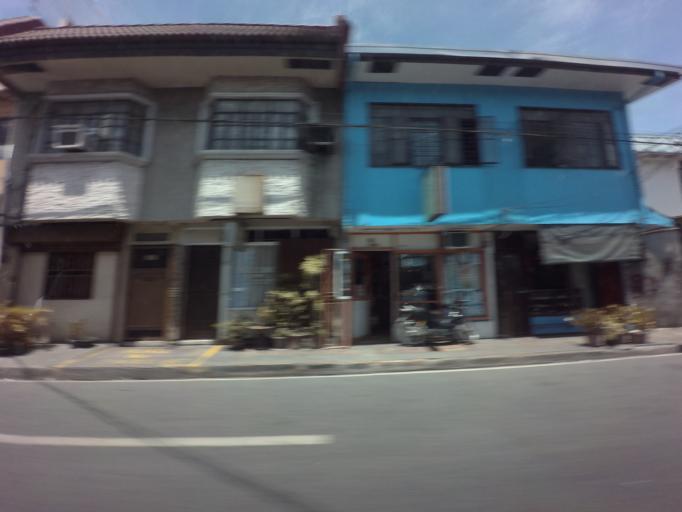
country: PH
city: Sambayanihan People's Village
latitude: 14.5035
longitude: 120.9934
